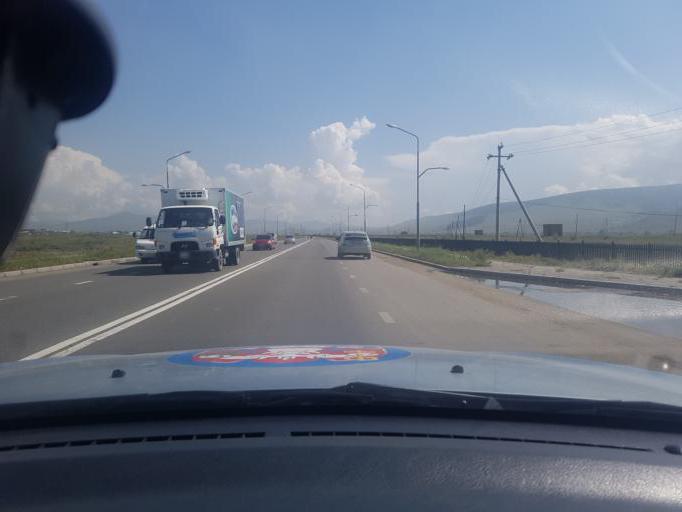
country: MN
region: Ulaanbaatar
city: Ulaanbaatar
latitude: 47.9031
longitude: 106.9804
